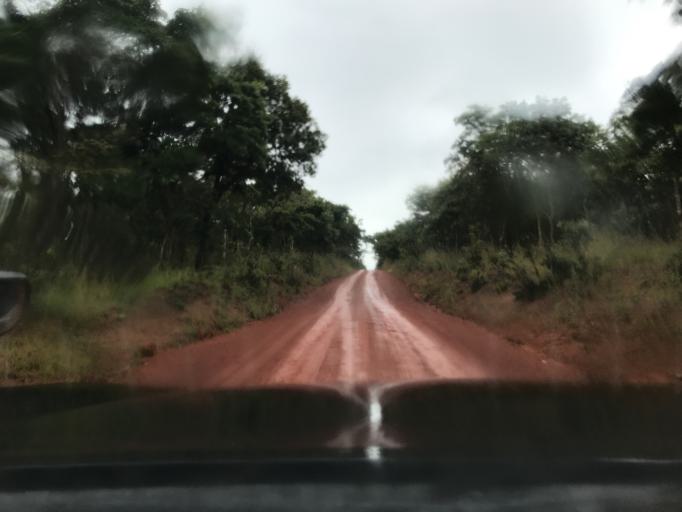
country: TZ
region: Kigoma
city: Uvinza
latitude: -5.2966
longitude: 30.3758
